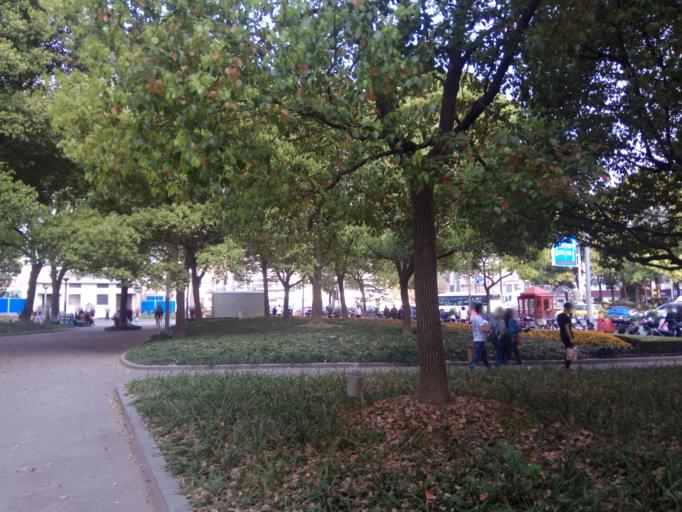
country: CN
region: Shanghai Shi
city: Changning
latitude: 31.2213
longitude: 121.4159
